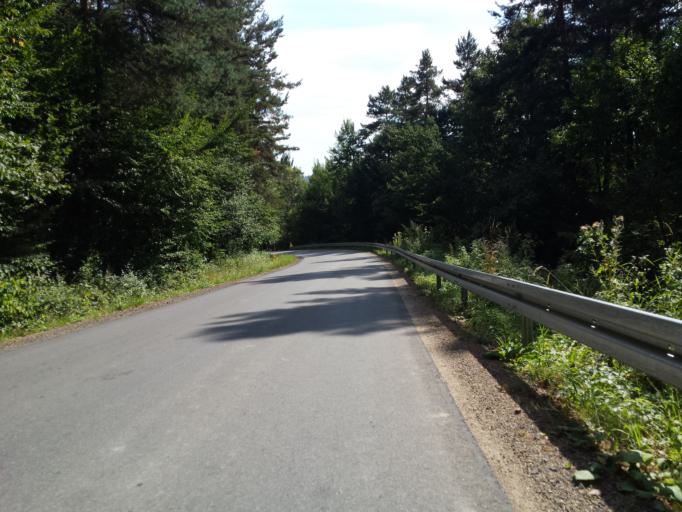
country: PL
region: Subcarpathian Voivodeship
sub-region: Powiat bieszczadzki
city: Ustrzyki Dolne
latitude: 49.5459
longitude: 22.5890
